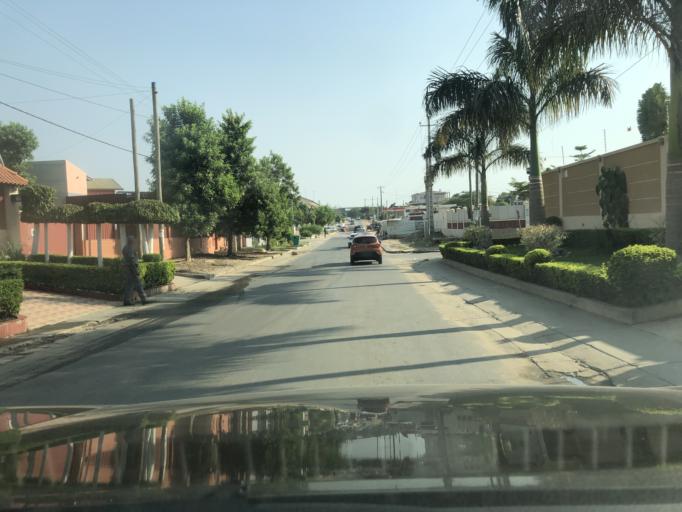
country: AO
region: Luanda
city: Luanda
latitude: -8.9100
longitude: 13.2275
